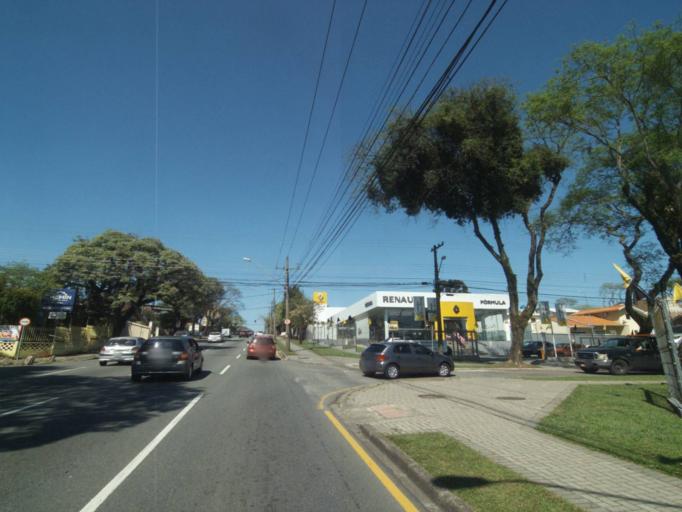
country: BR
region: Parana
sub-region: Curitiba
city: Curitiba
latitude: -25.3921
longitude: -49.2407
